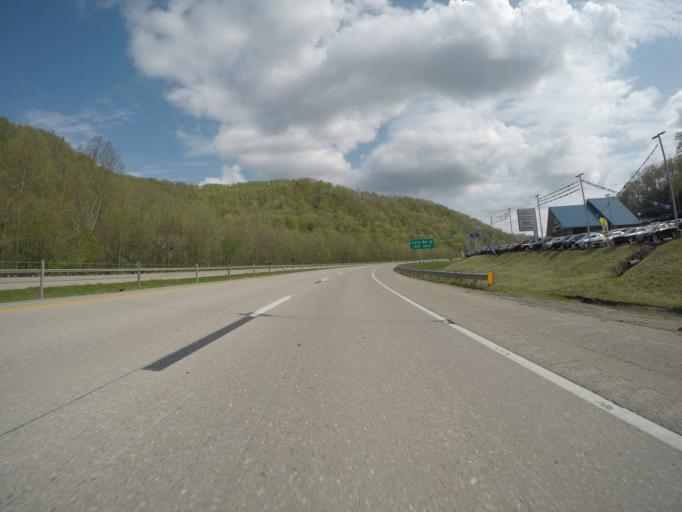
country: US
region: West Virginia
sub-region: Boone County
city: Madison
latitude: 38.1262
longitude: -81.8436
